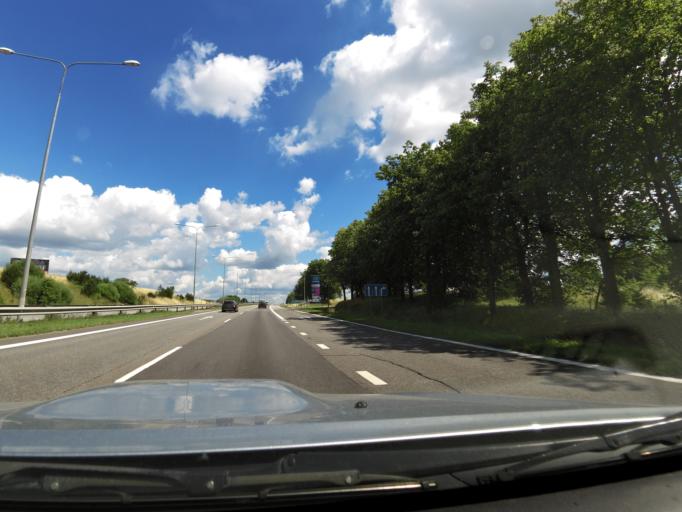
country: LT
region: Vilnius County
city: Elektrenai
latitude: 54.7875
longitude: 24.7123
